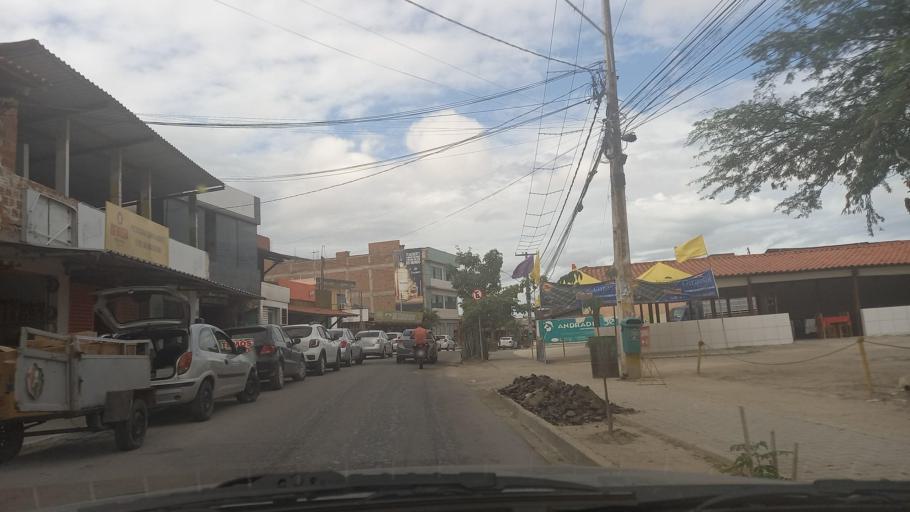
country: BR
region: Pernambuco
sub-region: Caruaru
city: Caruaru
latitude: -8.2907
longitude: -36.0292
